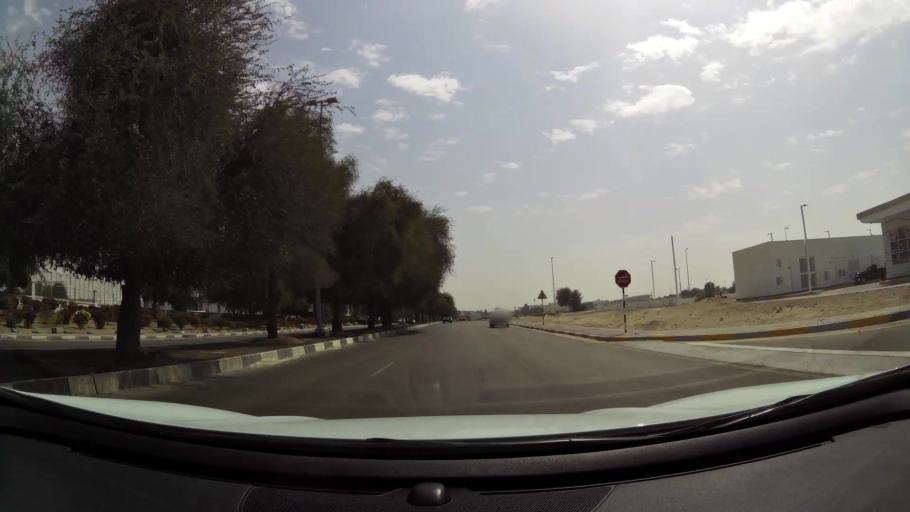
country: AE
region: Abu Dhabi
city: Abu Dhabi
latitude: 24.3039
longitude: 54.6226
